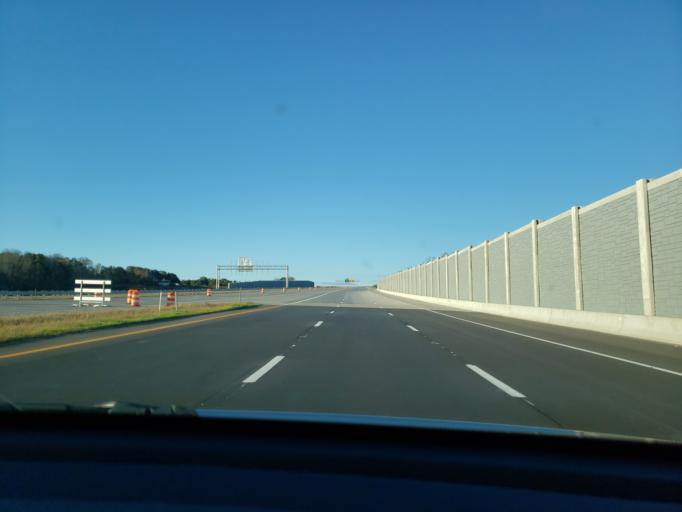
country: US
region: North Carolina
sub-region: Forsyth County
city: Kernersville
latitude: 36.1208
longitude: -80.1292
